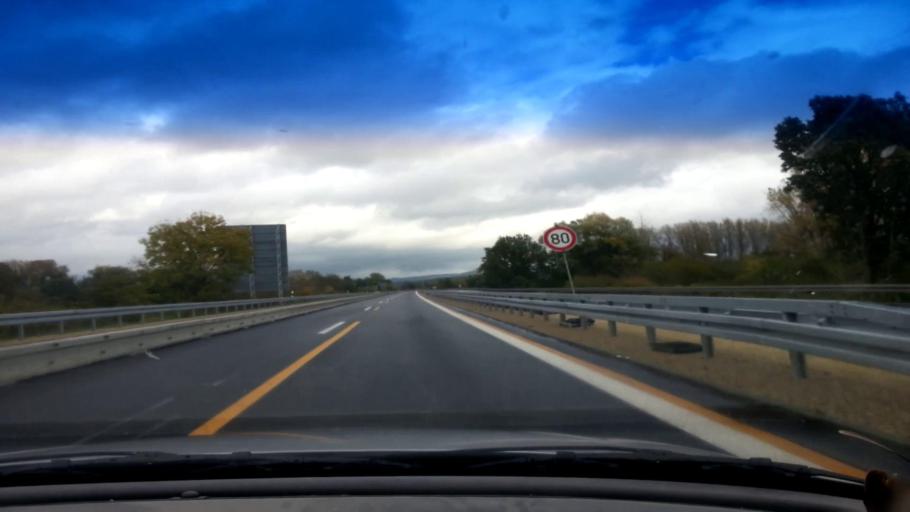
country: DE
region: Bavaria
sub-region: Upper Franconia
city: Gundelsheim
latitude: 49.9317
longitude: 10.9301
